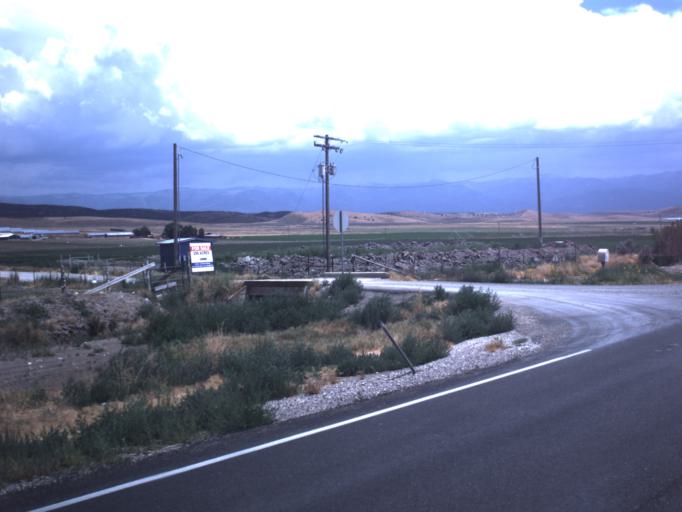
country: US
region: Utah
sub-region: Sanpete County
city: Fountain Green
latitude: 39.5925
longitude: -111.6179
